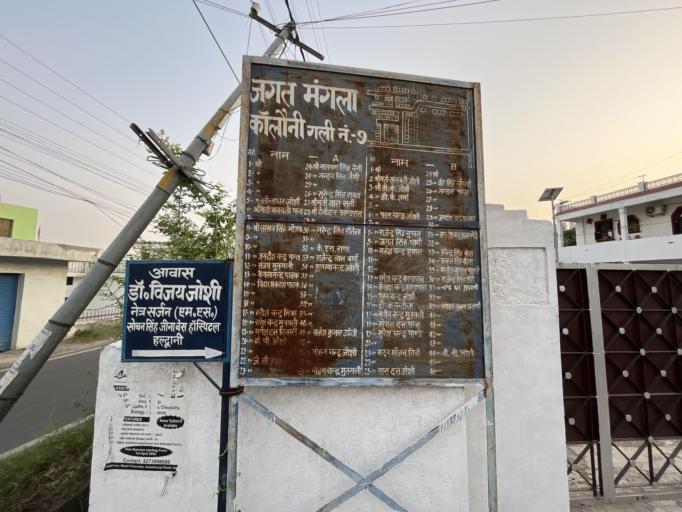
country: IN
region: Uttarakhand
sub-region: Naini Tal
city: Haldwani
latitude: 29.2233
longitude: 79.4934
